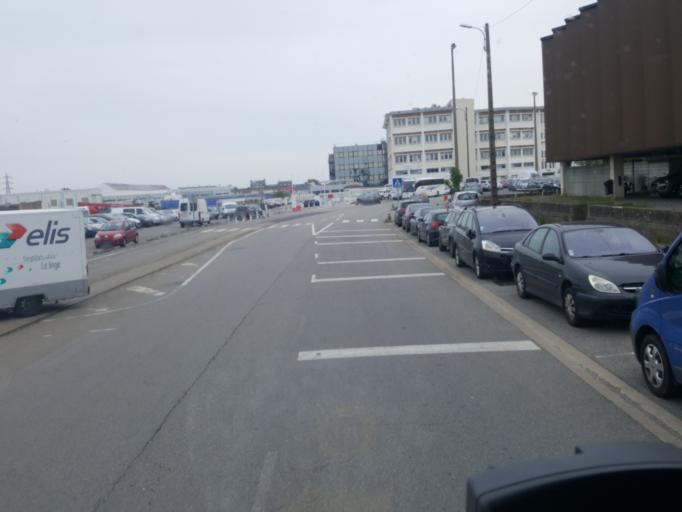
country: FR
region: Pays de la Loire
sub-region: Departement de la Loire-Atlantique
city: Saint-Nazaire
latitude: 47.2855
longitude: -2.1960
